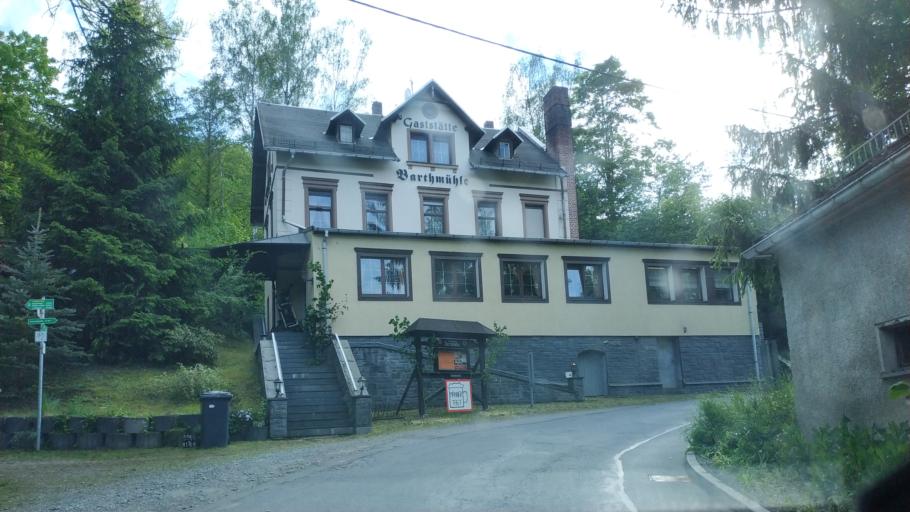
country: DE
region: Saxony
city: Pohl
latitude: 50.5568
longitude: 12.1622
